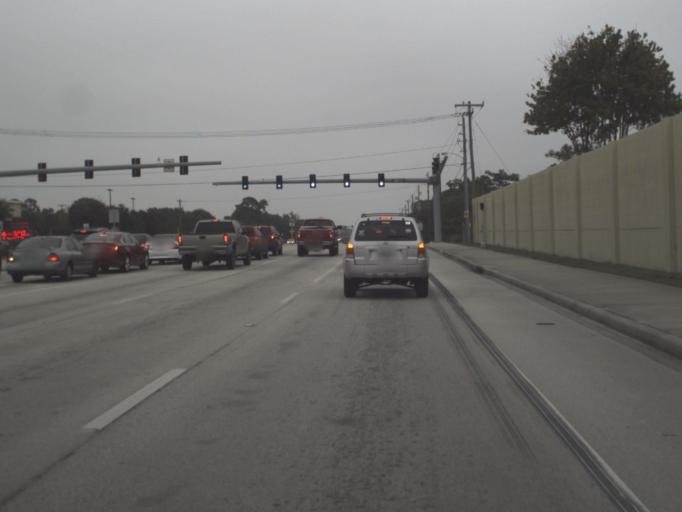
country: US
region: Florida
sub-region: Brevard County
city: West Melbourne
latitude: 28.0351
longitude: -80.6391
